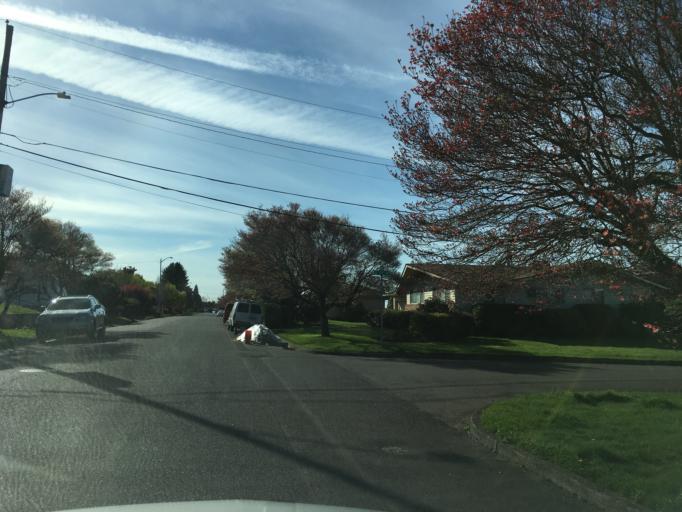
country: US
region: Oregon
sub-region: Multnomah County
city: Lents
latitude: 45.5460
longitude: -122.5294
